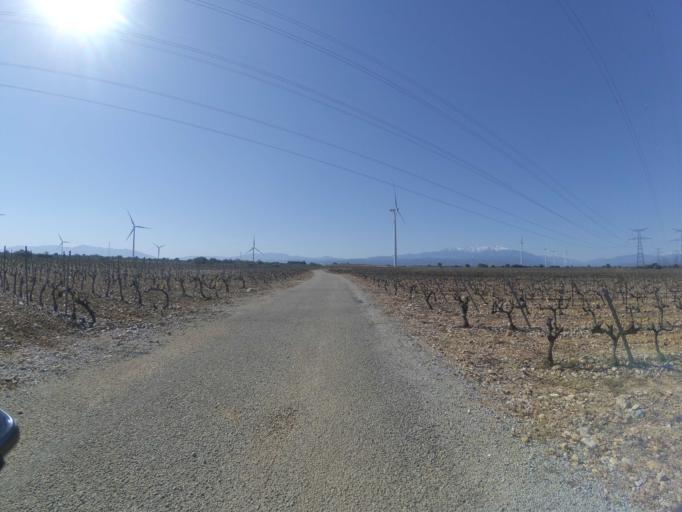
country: FR
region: Languedoc-Roussillon
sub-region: Departement des Pyrenees-Orientales
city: Pezilla-la-Riviere
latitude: 42.7239
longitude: 2.7707
